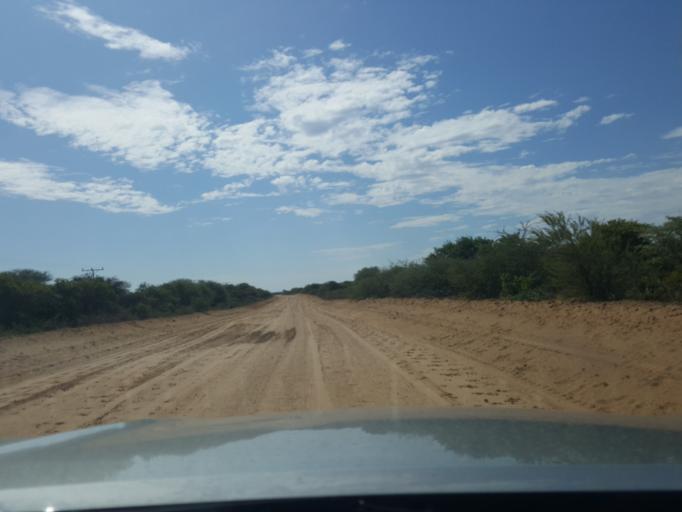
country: BW
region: Kweneng
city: Khudumelapye
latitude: -23.8693
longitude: 24.8951
